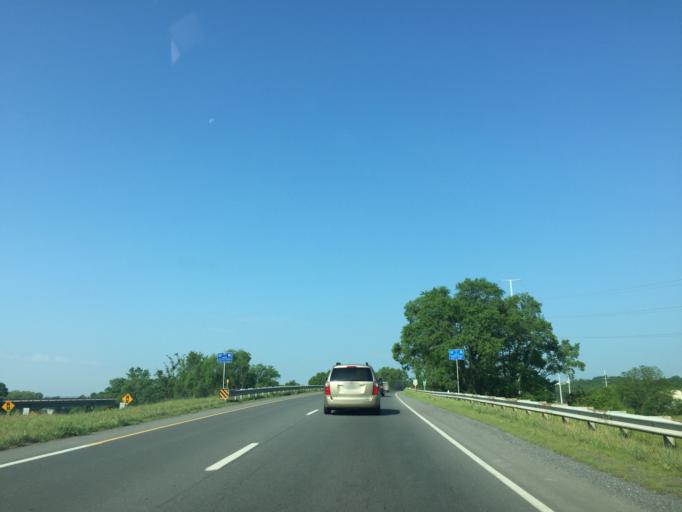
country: US
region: Virginia
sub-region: City of Winchester
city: Winchester
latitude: 39.2141
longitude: -78.1458
